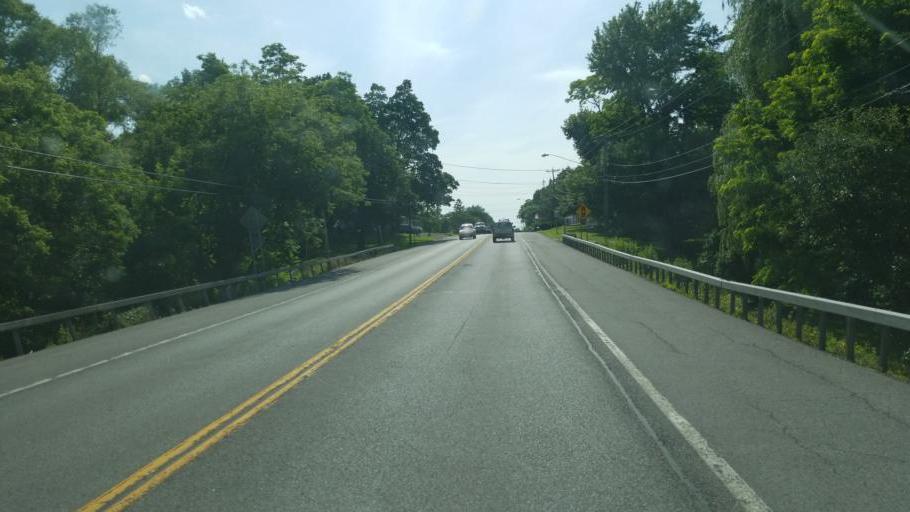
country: US
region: New York
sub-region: Monroe County
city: Honeoye Falls
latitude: 42.9059
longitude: -77.5353
